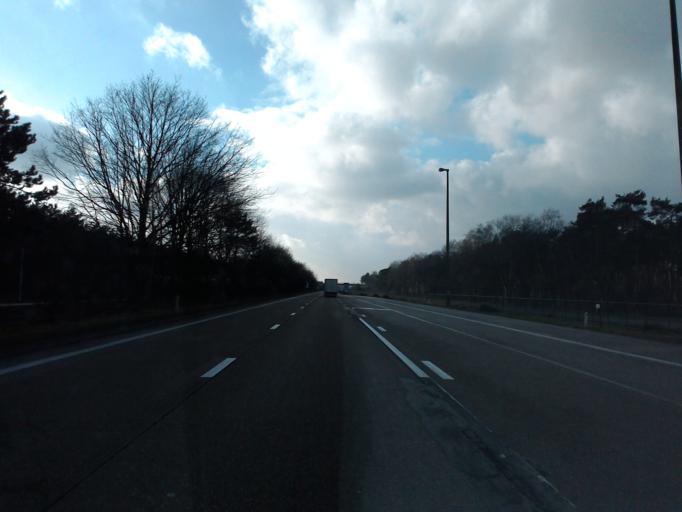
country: NL
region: North Brabant
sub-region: Gemeente Bladel en Netersel
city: Bladel
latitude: 51.3117
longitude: 5.1865
